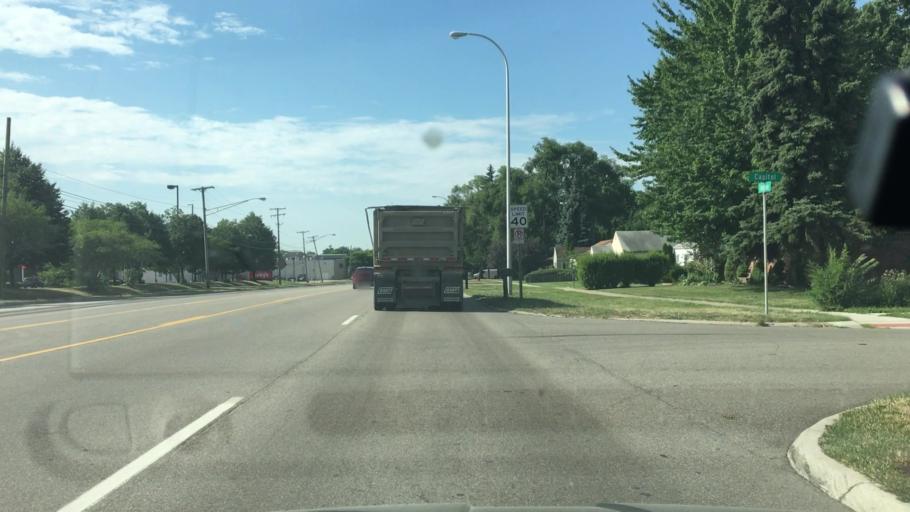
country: US
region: Michigan
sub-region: Wayne County
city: Redford
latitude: 42.3747
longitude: -83.3139
